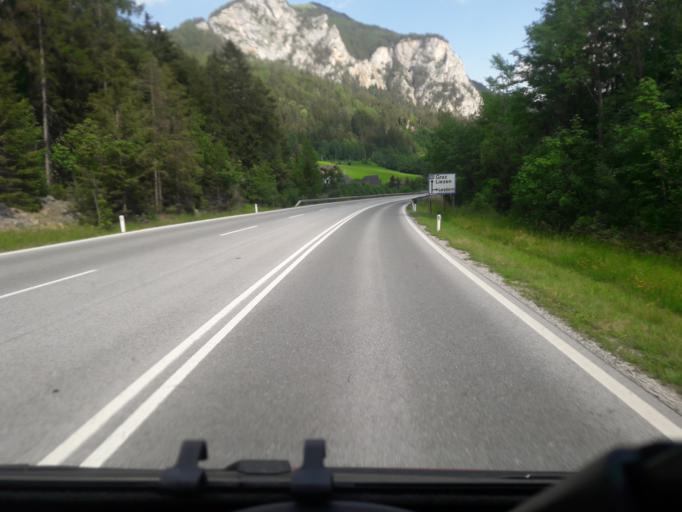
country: AT
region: Styria
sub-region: Politischer Bezirk Liezen
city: Tauplitz
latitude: 47.5464
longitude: 14.0345
